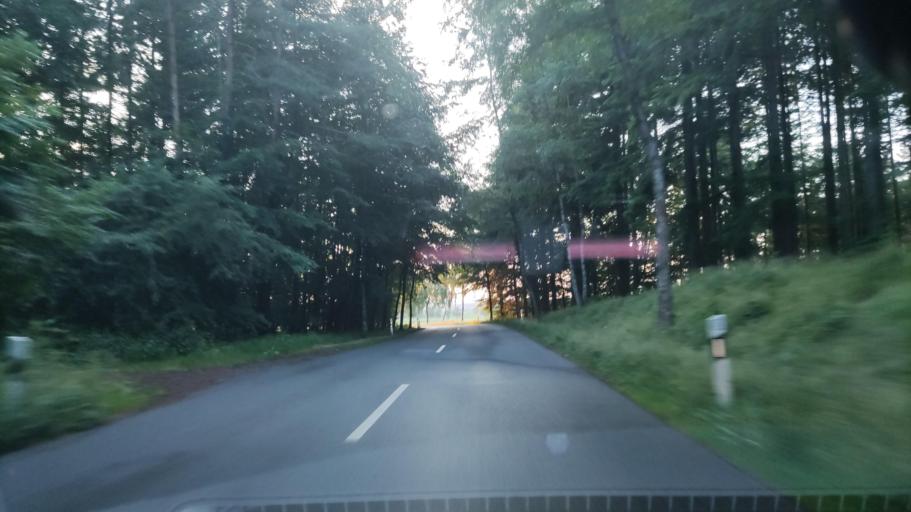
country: DE
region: Lower Saxony
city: Bispingen
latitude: 53.1249
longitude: 10.0508
